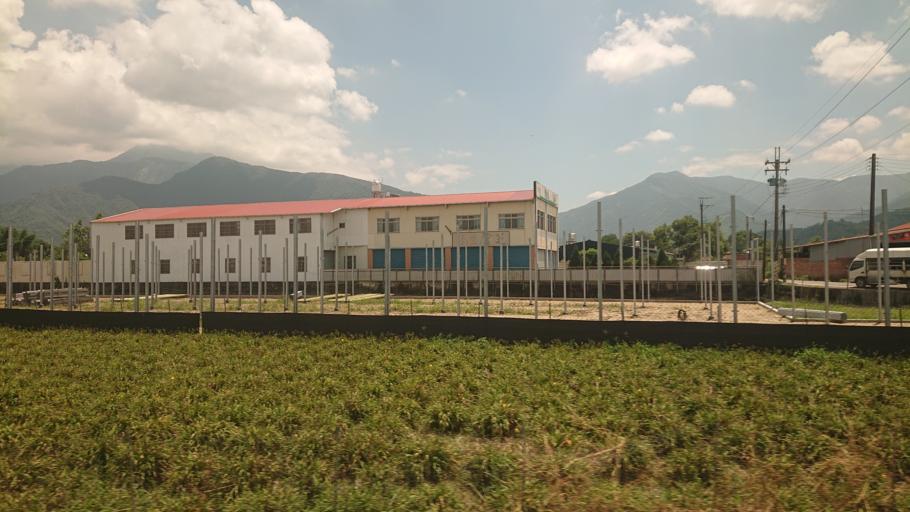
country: TW
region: Taiwan
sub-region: Nantou
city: Puli
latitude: 23.9785
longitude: 120.9612
